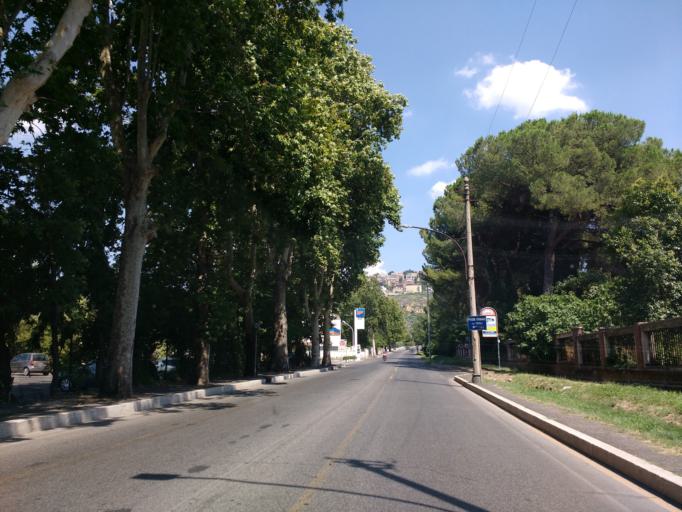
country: IT
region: Latium
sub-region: Citta metropolitana di Roma Capitale
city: Villa Adriana
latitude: 41.9566
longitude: 12.7789
